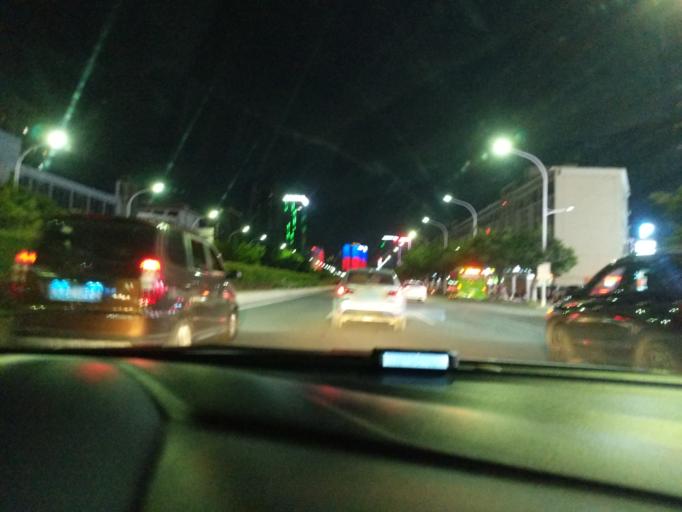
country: CN
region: Guangdong
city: Nansha
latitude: 22.8037
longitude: 113.5406
